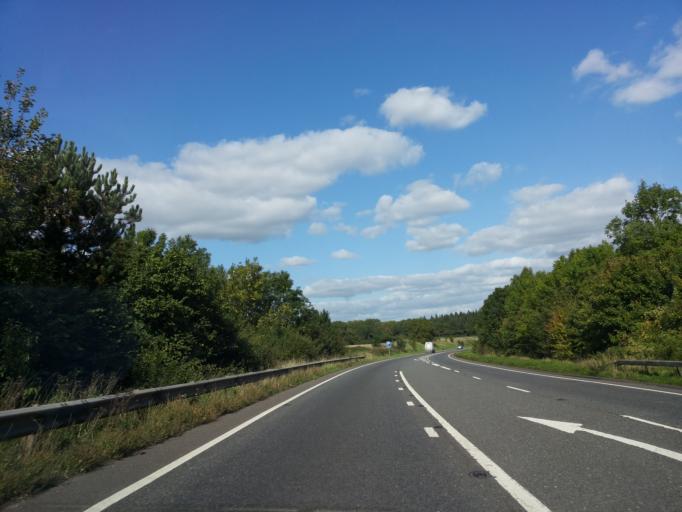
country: GB
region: England
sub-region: Wiltshire
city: Corsley
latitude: 51.2035
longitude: -2.2166
